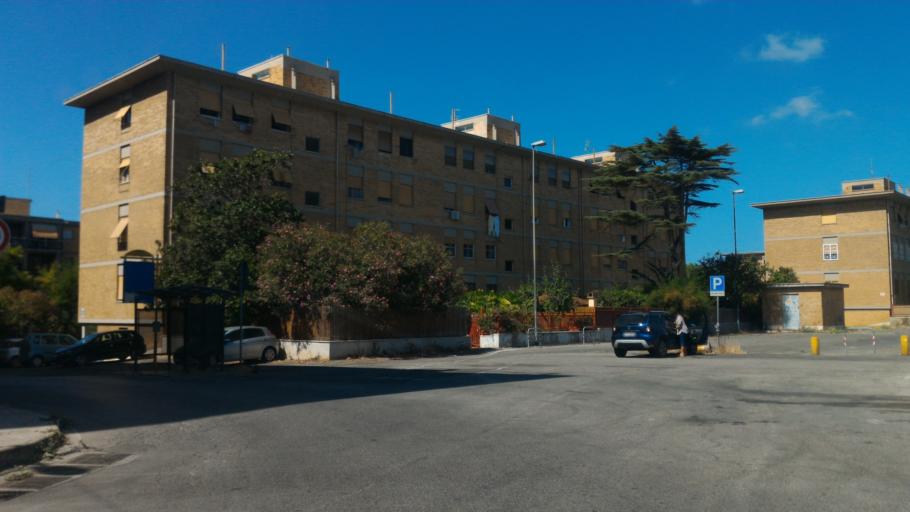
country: IT
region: Latium
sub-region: Citta metropolitana di Roma Capitale
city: Civitavecchia
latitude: 42.0831
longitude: 11.8126
